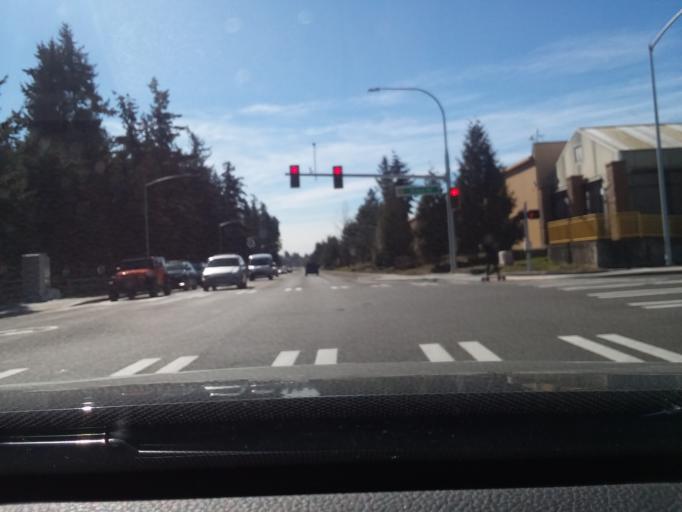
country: US
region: Washington
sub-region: Pierce County
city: Puyallup
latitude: 47.1622
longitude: -122.2878
